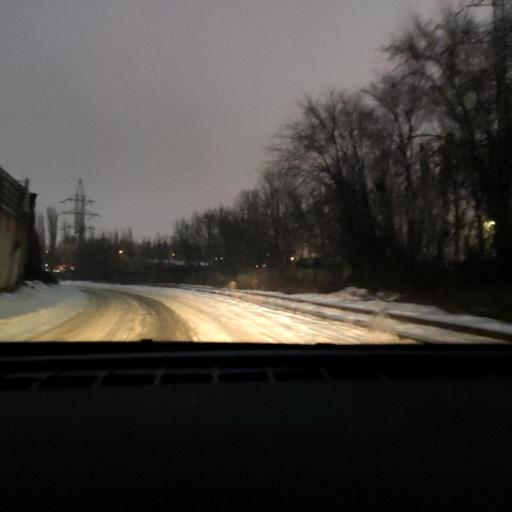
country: RU
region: Voronezj
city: Voronezh
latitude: 51.6480
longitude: 39.2647
